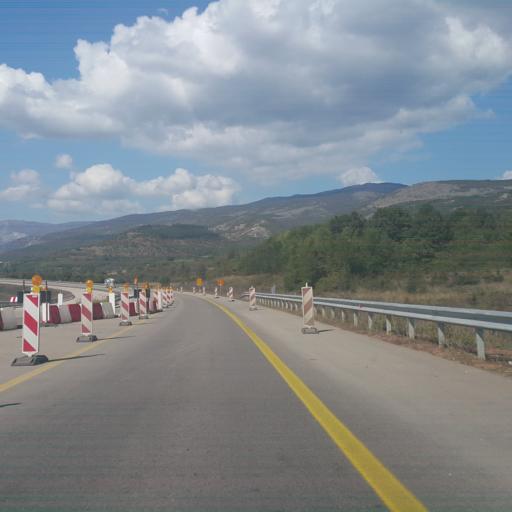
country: RS
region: Central Serbia
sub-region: Pirotski Okrug
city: Bela Palanka
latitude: 43.2533
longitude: 22.2694
